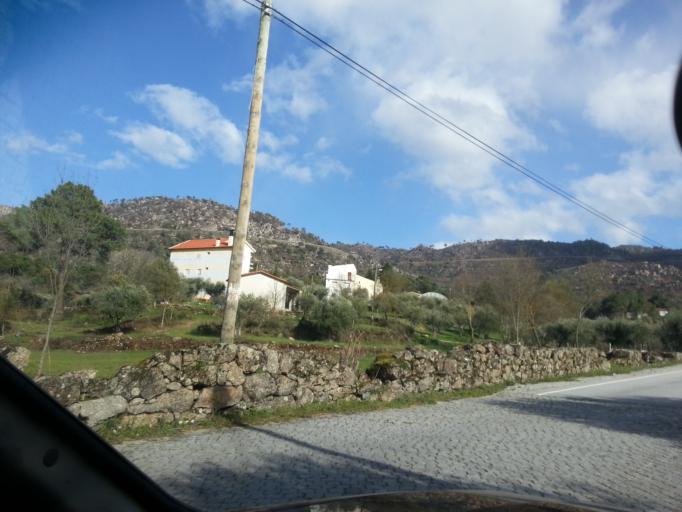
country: PT
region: Guarda
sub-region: Guarda
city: Guarda
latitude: 40.6016
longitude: -7.2938
